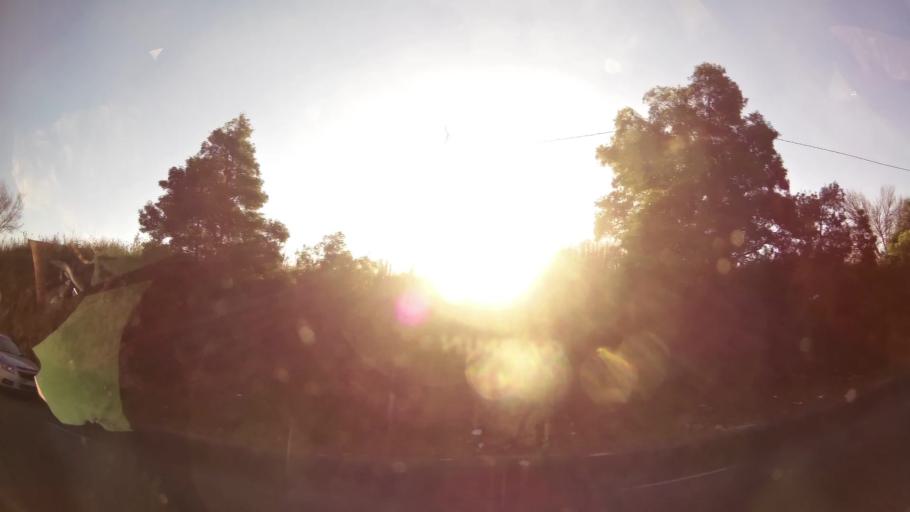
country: ZA
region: Gauteng
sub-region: City of Johannesburg Metropolitan Municipality
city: Johannesburg
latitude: -26.2170
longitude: 27.9823
